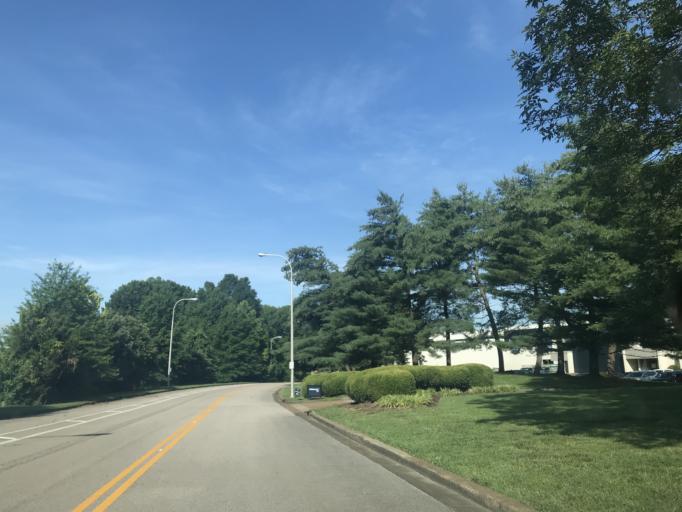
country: US
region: Tennessee
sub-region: Davidson County
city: Nashville
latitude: 36.1936
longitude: -86.8207
